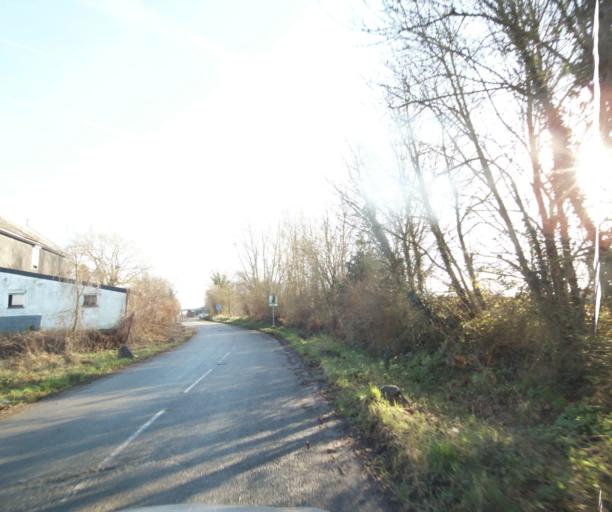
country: FR
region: Nord-Pas-de-Calais
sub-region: Departement du Nord
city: Curgies
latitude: 50.3227
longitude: 3.6006
